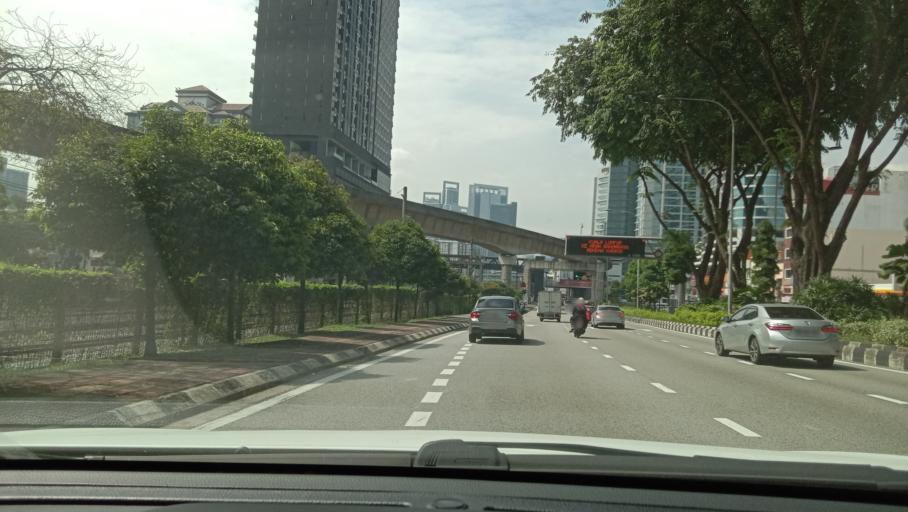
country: MY
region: Kuala Lumpur
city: Kuala Lumpur
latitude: 3.1299
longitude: 101.6810
